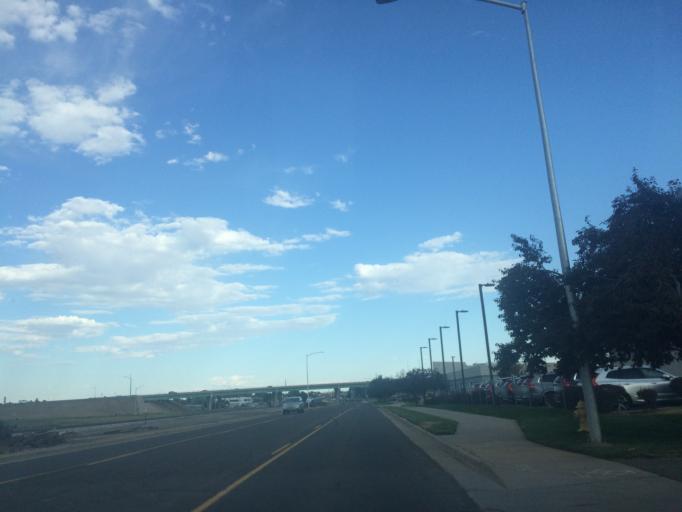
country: US
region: Colorado
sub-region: Broomfield County
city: Broomfield
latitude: 39.9200
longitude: -105.0946
